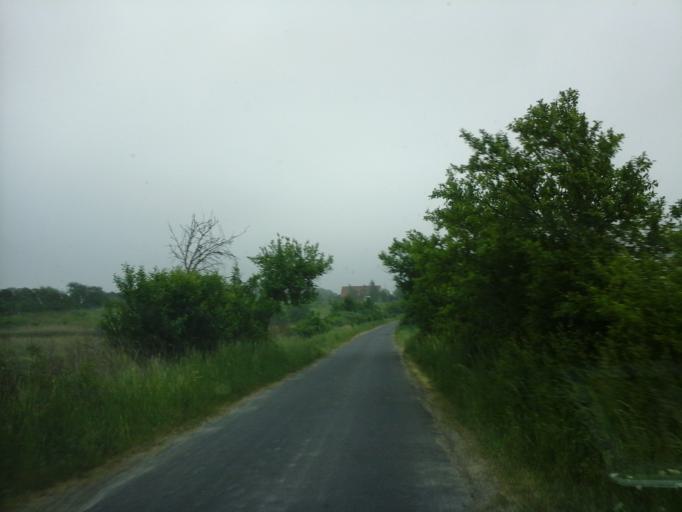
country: PL
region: West Pomeranian Voivodeship
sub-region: Powiat choszczenski
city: Pelczyce
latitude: 53.0178
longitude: 15.3346
